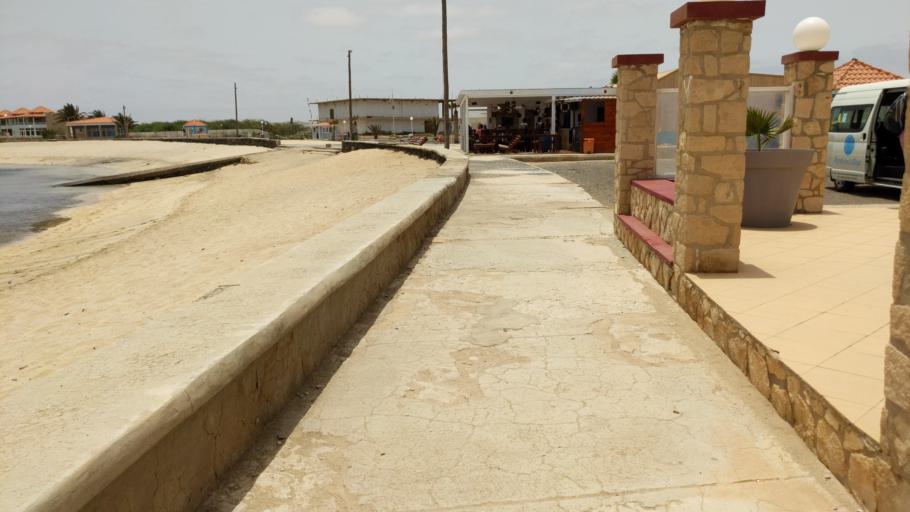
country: CV
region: Sal
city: Espargos
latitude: 16.6777
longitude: -22.9355
